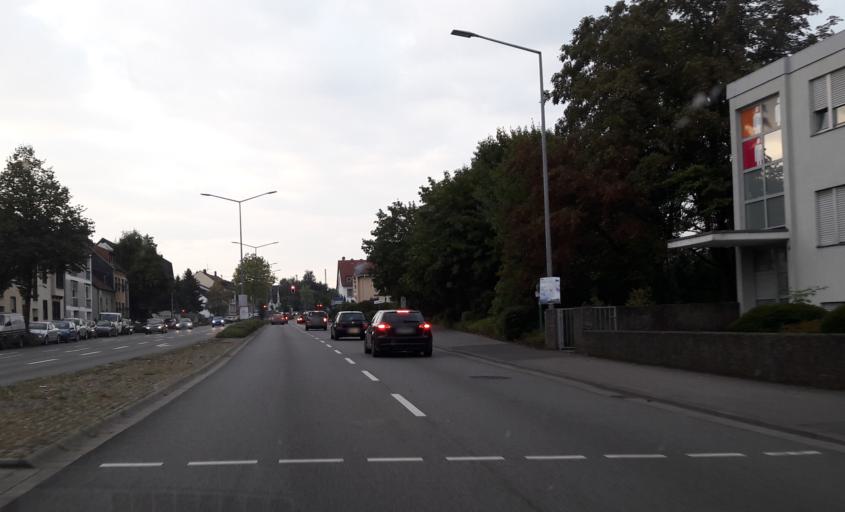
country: DE
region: Saarland
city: Homburg
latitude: 49.3196
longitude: 7.3341
